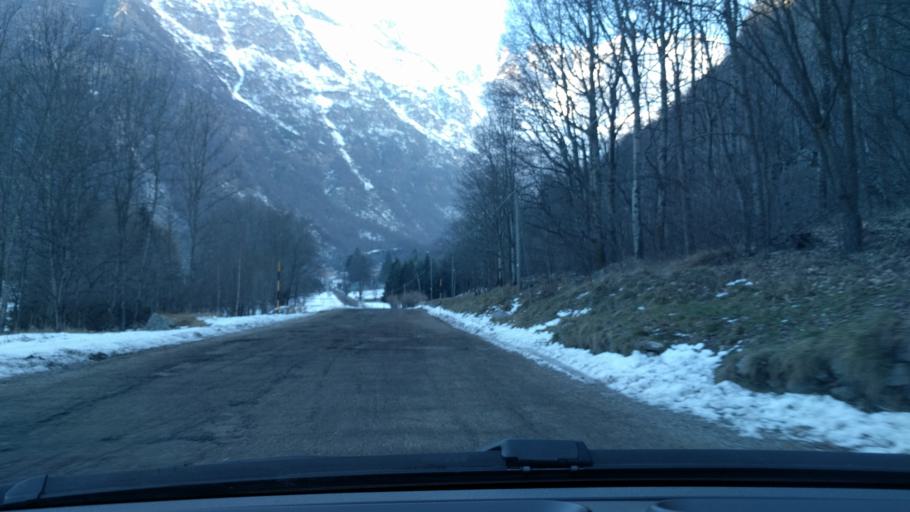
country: IT
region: Piedmont
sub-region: Provincia di Torino
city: Groscavallo
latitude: 45.3653
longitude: 7.2301
